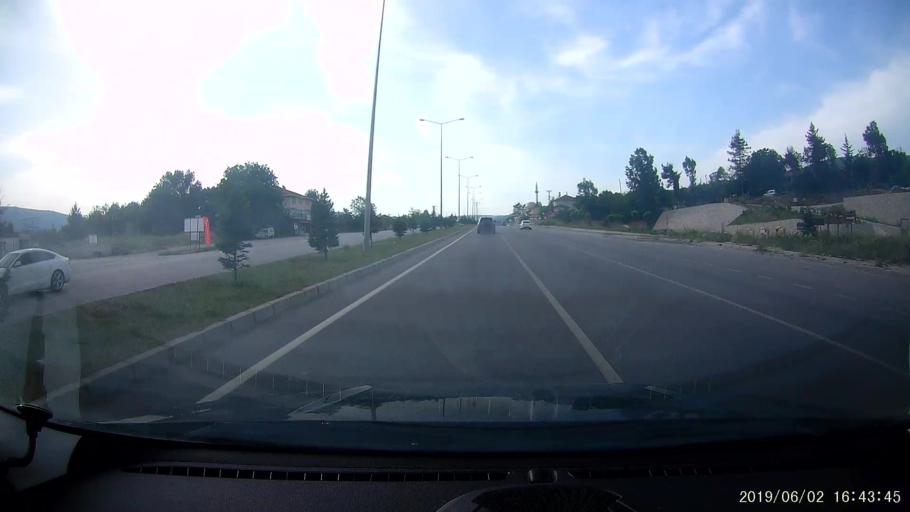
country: TR
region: Samsun
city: Kavak
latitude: 41.1403
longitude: 36.1215
